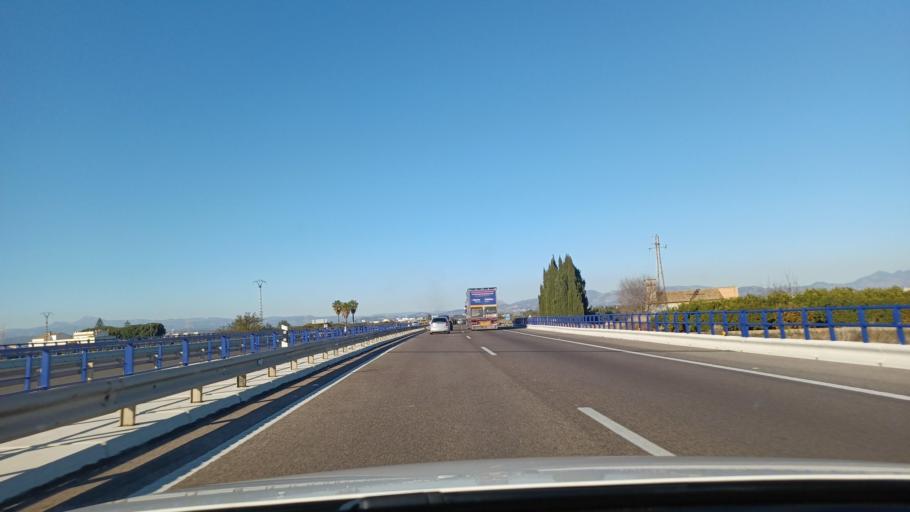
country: ES
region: Valencia
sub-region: Provincia de Castello
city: Alquerias del Nino Perdido
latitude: 39.9097
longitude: -0.1351
